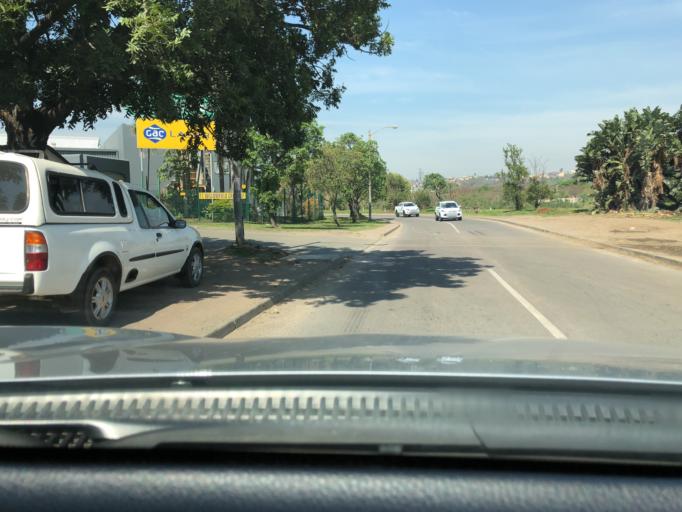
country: ZA
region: KwaZulu-Natal
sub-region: eThekwini Metropolitan Municipality
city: Berea
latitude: -29.8050
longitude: 30.9955
